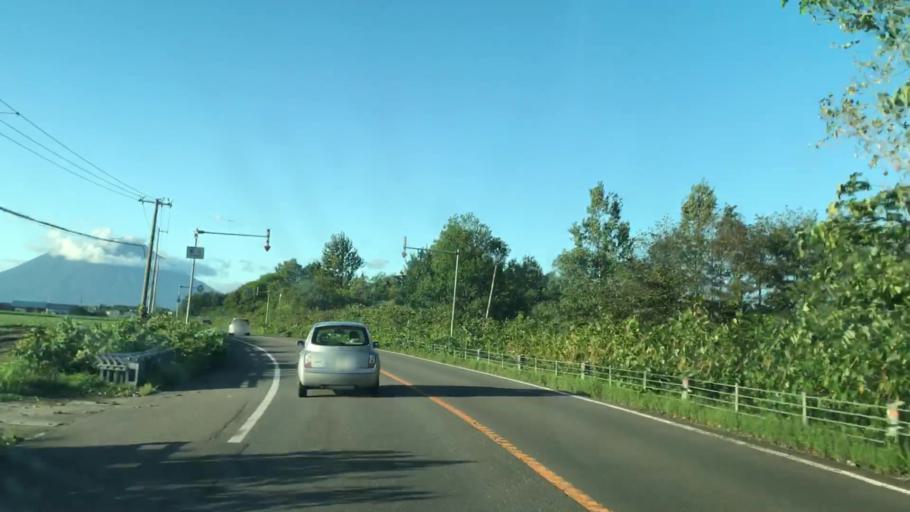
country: JP
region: Hokkaido
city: Date
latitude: 42.6500
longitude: 140.8109
